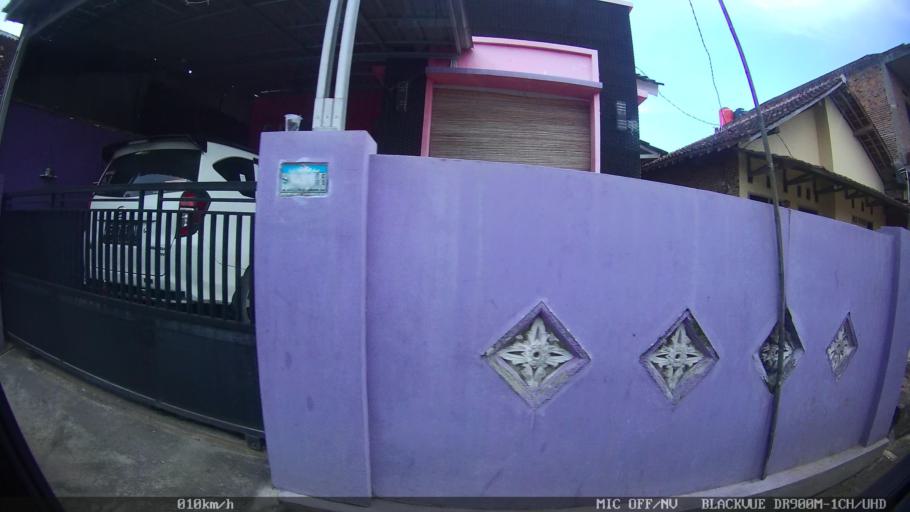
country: ID
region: Lampung
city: Kedaton
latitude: -5.3992
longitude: 105.2337
